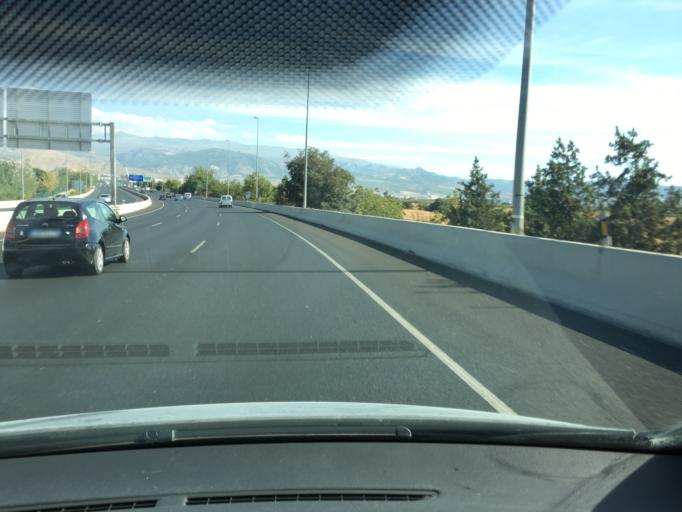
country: ES
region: Andalusia
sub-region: Provincia de Granada
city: Maracena
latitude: 37.1861
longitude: -3.6317
